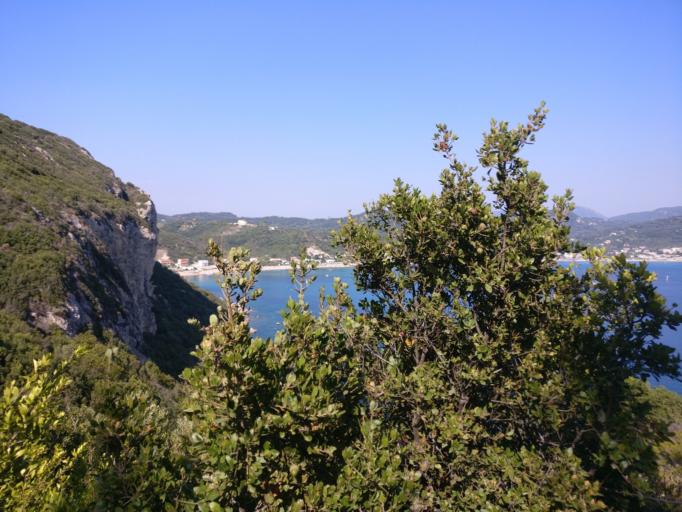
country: GR
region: Ionian Islands
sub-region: Nomos Kerkyras
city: Agios Georgis
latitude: 39.7169
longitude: 19.6584
